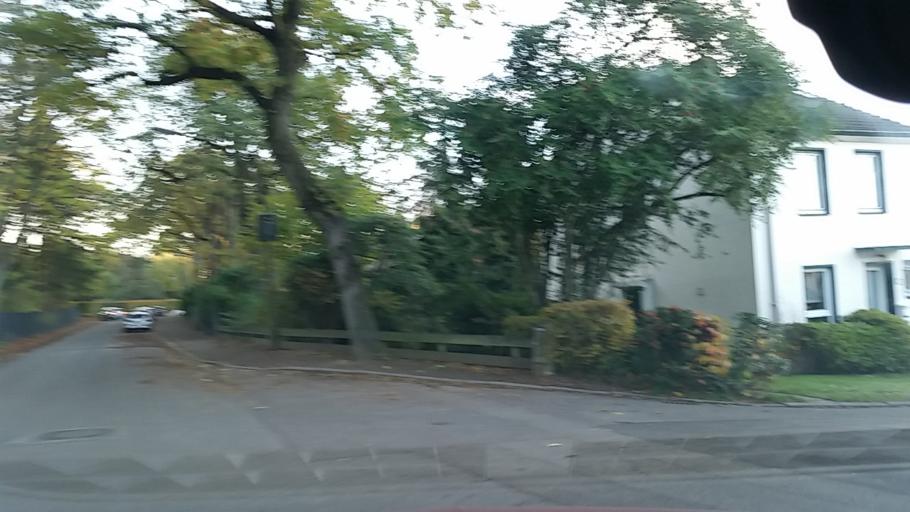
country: DE
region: Schleswig-Holstein
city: Rellingen
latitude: 53.5676
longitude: 9.7886
